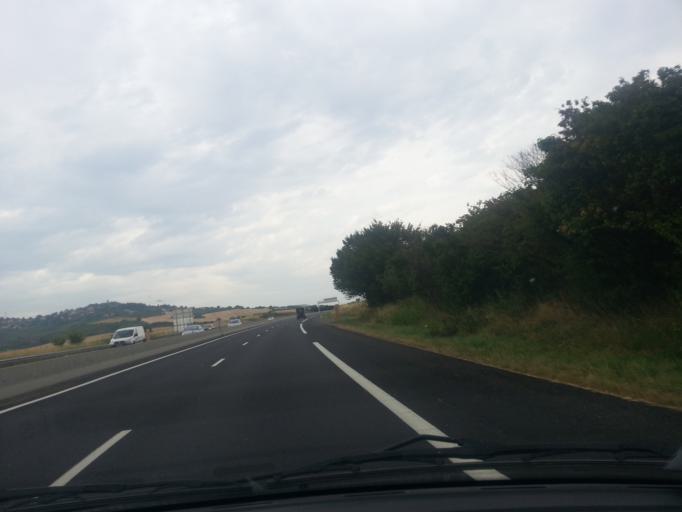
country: FR
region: Auvergne
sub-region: Departement du Puy-de-Dome
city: Tallende
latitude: 45.6691
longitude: 3.1433
